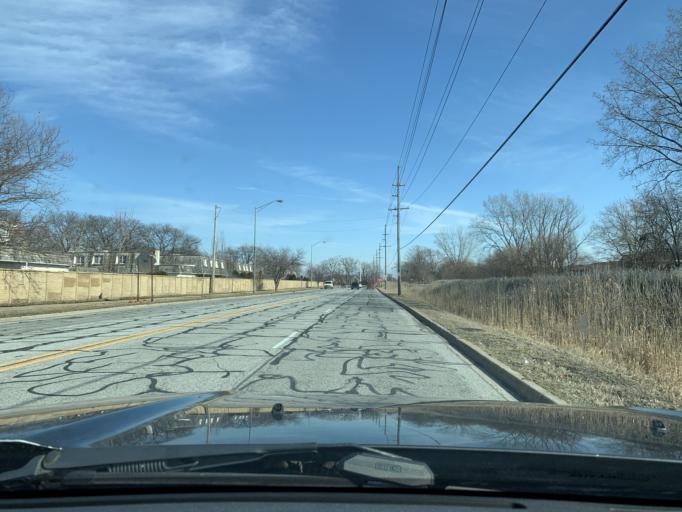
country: US
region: Indiana
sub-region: Lake County
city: Munster
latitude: 41.5385
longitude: -87.4975
